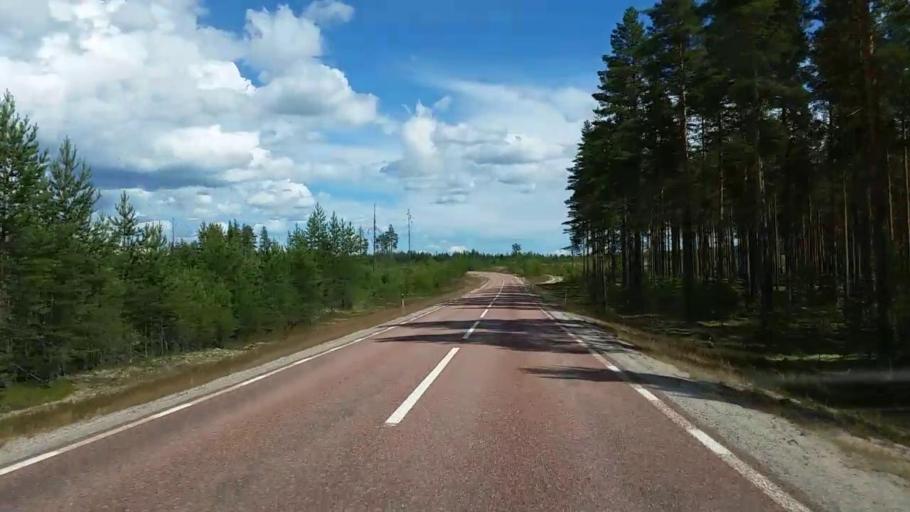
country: SE
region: Gaevleborg
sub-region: Ovanakers Kommun
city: Edsbyn
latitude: 61.3430
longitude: 15.5564
